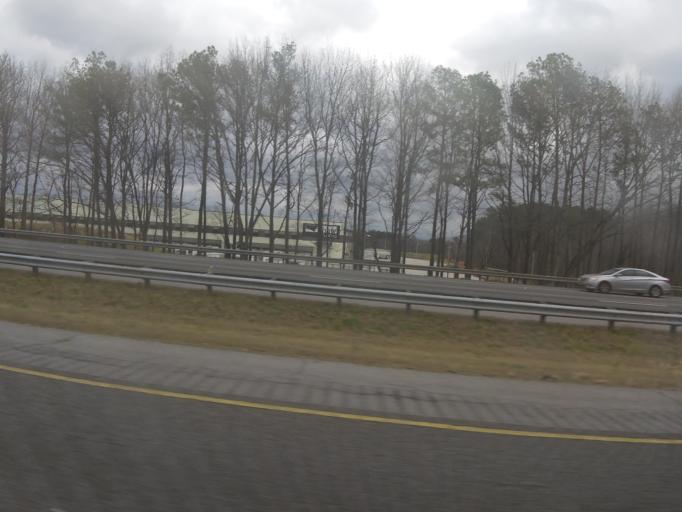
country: US
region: Georgia
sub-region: Whitfield County
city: Dalton
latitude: 34.6770
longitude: -84.9990
